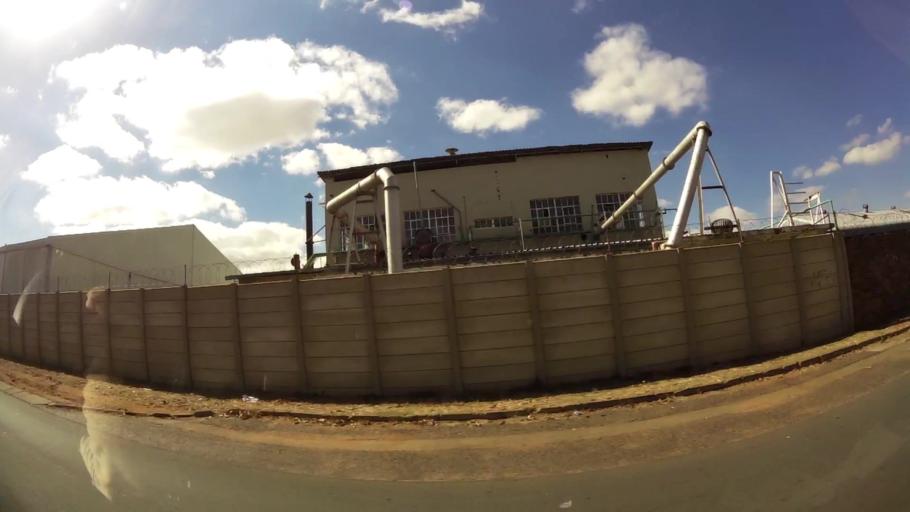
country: ZA
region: Gauteng
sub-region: West Rand District Municipality
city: Krugersdorp
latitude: -26.1159
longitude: 27.8148
